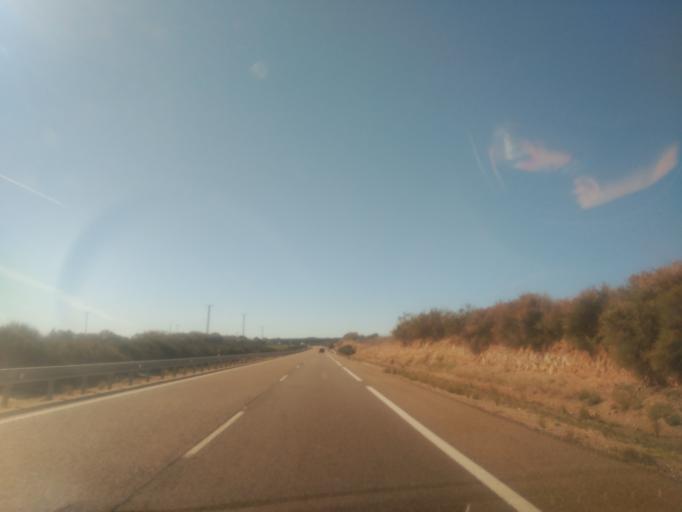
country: ES
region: Castille and Leon
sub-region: Provincia de Valladolid
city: Alaejos
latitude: 41.3133
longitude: -5.2221
